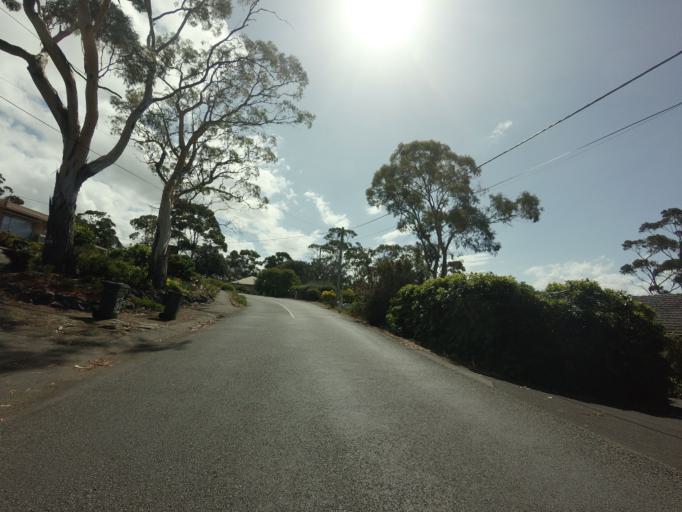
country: AU
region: Tasmania
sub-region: Hobart
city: Dynnyrne
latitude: -42.9111
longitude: 147.3231
